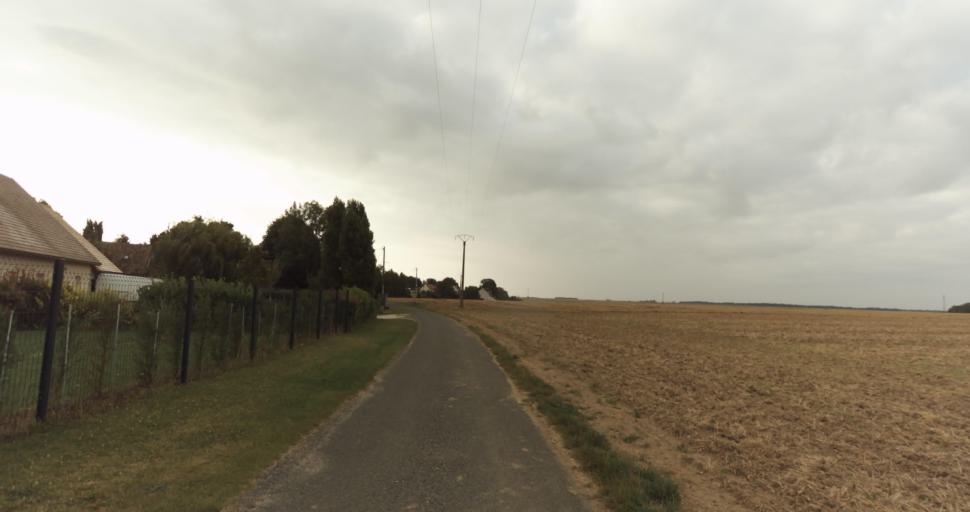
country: FR
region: Haute-Normandie
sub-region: Departement de l'Eure
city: Saint-Germain-sur-Avre
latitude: 48.7961
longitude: 1.2850
